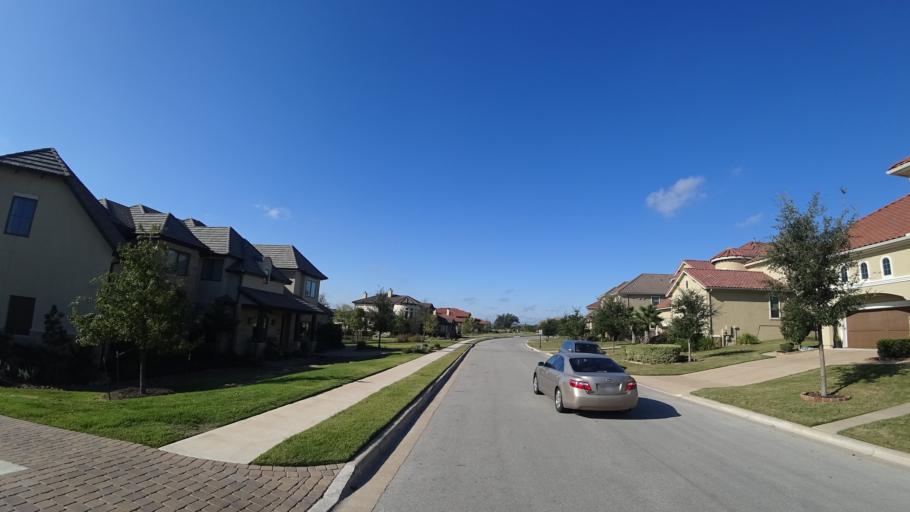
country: US
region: Texas
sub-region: Travis County
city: Bee Cave
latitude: 30.3442
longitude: -97.8937
